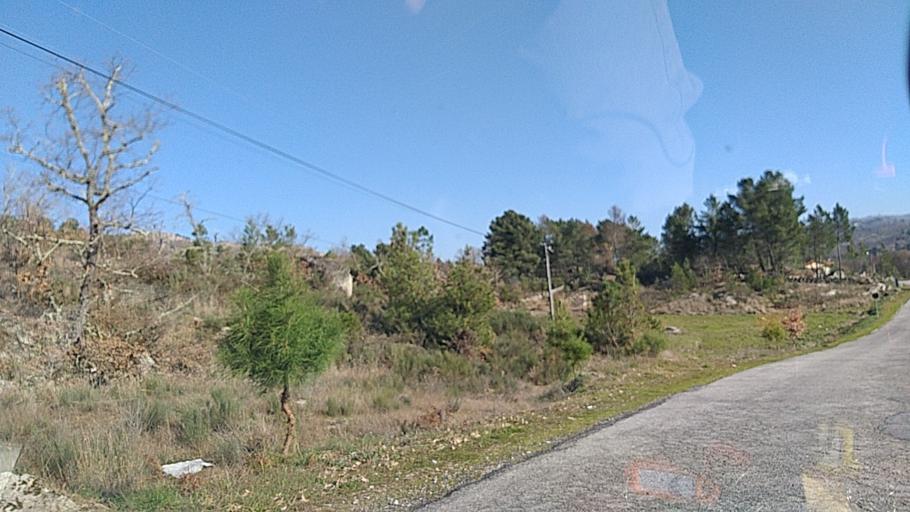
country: PT
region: Guarda
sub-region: Celorico da Beira
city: Celorico da Beira
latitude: 40.6608
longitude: -7.4628
